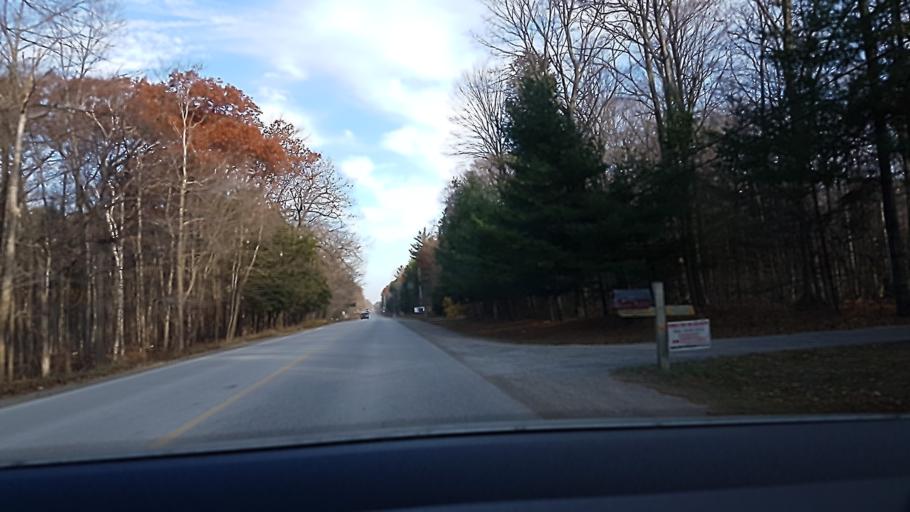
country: CA
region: Ontario
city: Barrie
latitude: 44.3930
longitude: -79.5455
